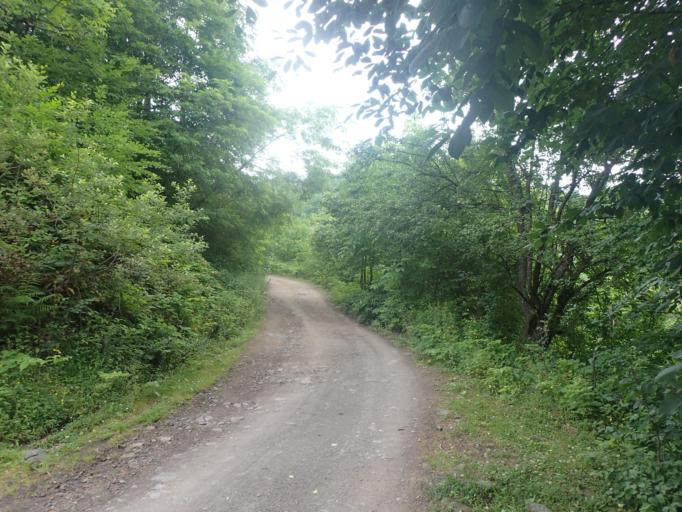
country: TR
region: Ordu
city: Akkus
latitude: 40.8678
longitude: 37.0074
